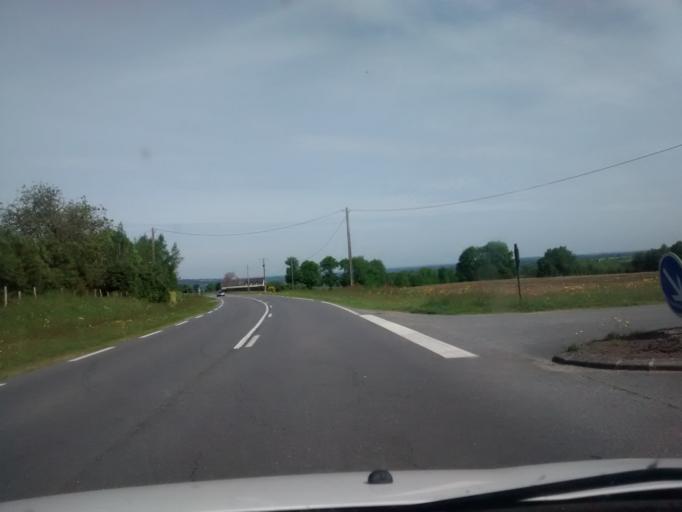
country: FR
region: Brittany
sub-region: Departement d'Ille-et-Vilaine
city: Tremblay
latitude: 48.4355
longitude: -1.4625
